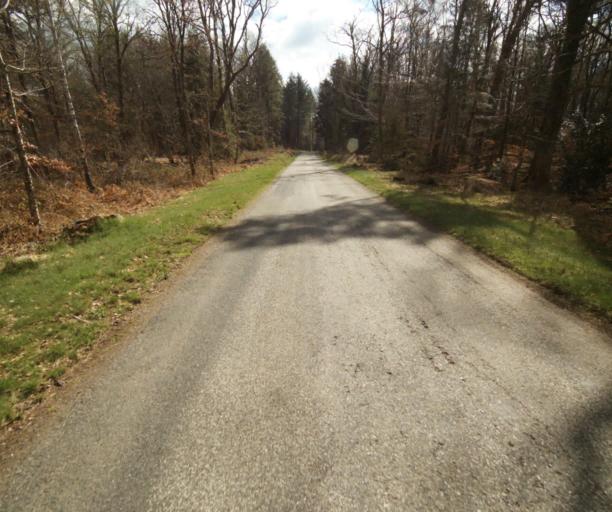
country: FR
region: Limousin
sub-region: Departement de la Correze
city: Correze
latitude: 45.2481
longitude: 1.9376
